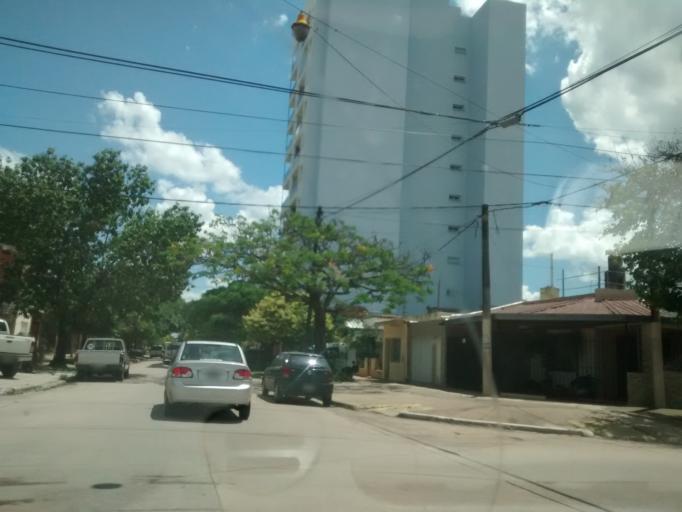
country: AR
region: Chaco
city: Resistencia
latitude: -27.4573
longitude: -58.9900
